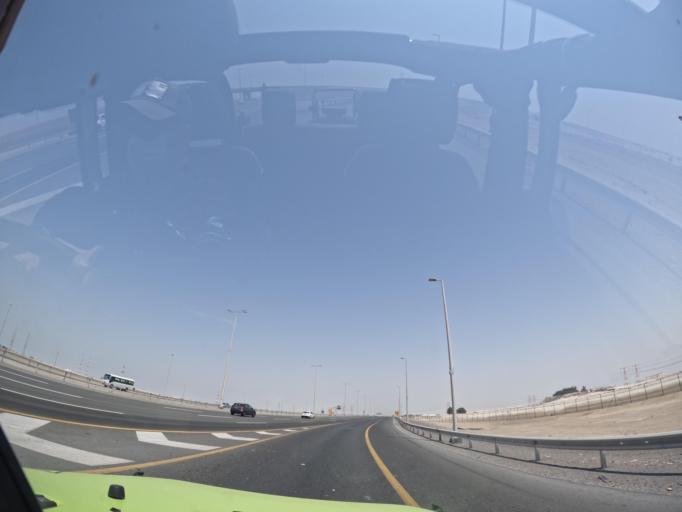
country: AE
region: Abu Dhabi
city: Abu Dhabi
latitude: 24.2138
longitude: 54.4169
